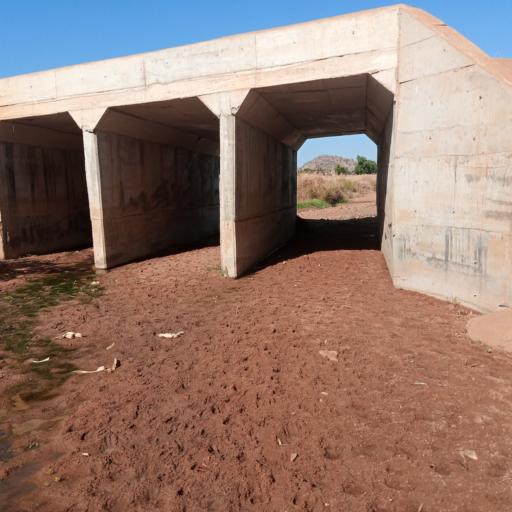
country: NG
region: Adamawa
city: Holma
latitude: 10.0119
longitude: 13.0951
